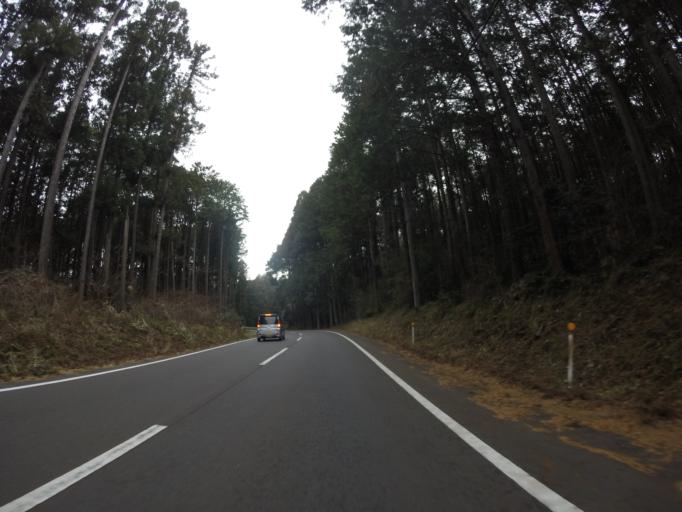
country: JP
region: Shizuoka
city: Fujinomiya
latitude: 35.2398
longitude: 138.5729
